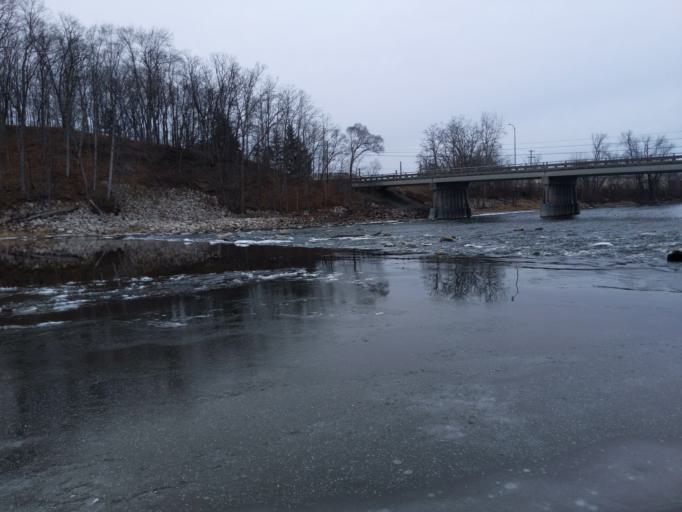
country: US
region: Michigan
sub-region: Ionia County
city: Portland
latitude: 42.9812
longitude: -84.9497
